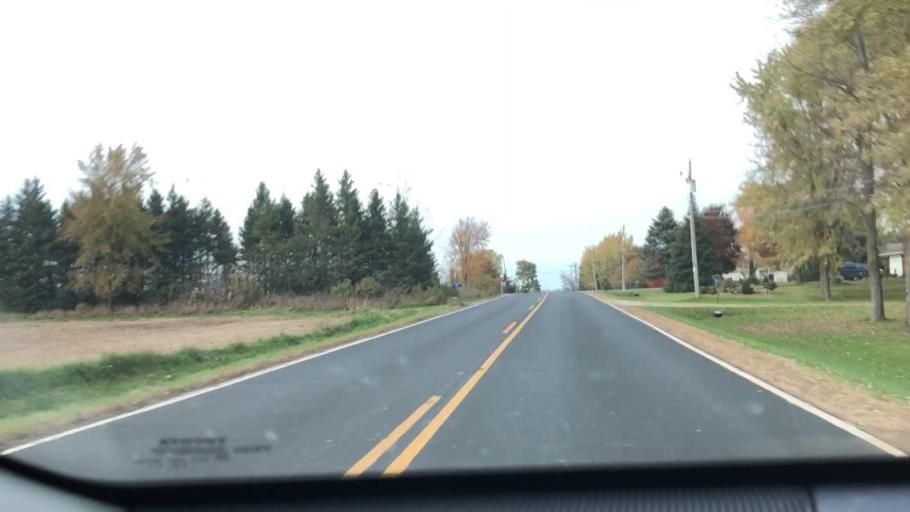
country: US
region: Wisconsin
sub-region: Outagamie County
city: Seymour
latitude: 44.4973
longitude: -88.3495
